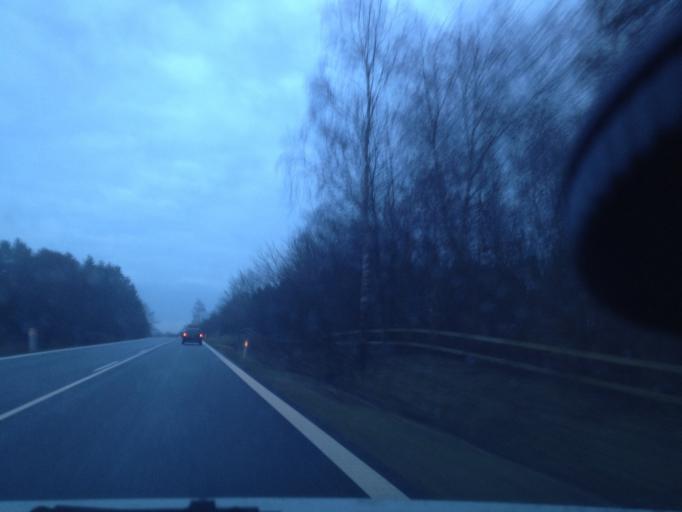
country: DK
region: Capital Region
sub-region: Rudersdal Kommune
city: Birkerod
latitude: 55.8956
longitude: 12.4293
